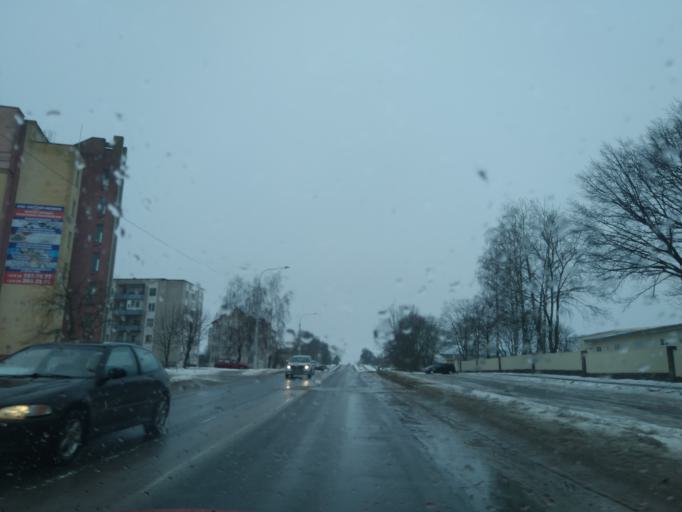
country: BY
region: Minsk
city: Nyasvizh
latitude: 53.2296
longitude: 26.6600
